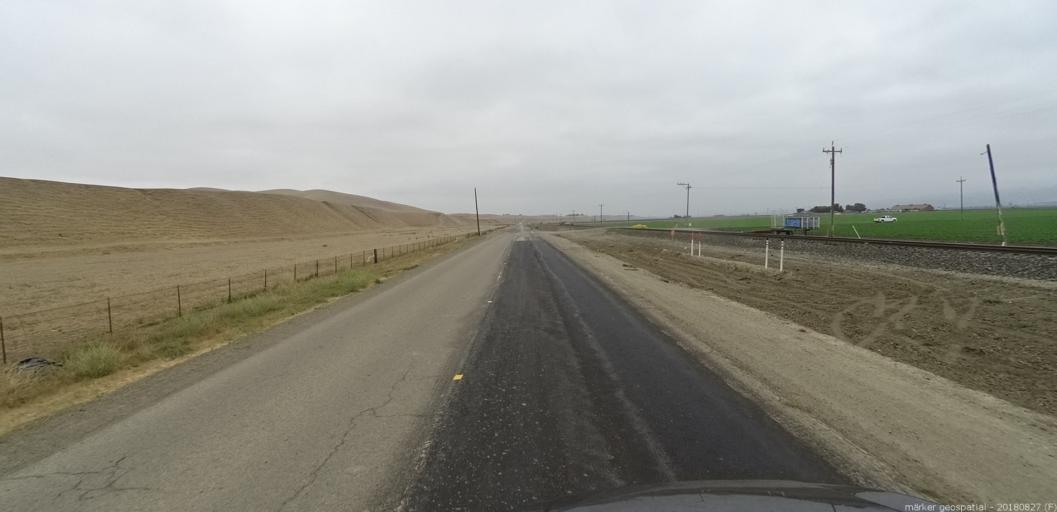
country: US
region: California
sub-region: Monterey County
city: Greenfield
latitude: 36.3052
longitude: -121.1635
